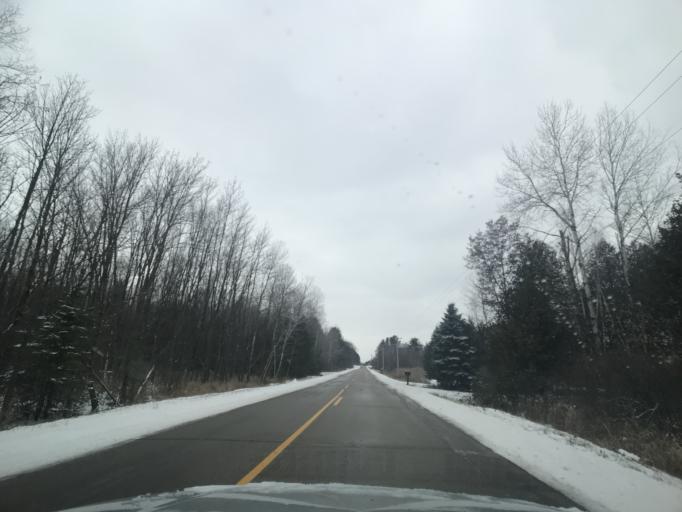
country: US
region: Wisconsin
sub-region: Brown County
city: Suamico
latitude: 44.7063
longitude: -88.0957
